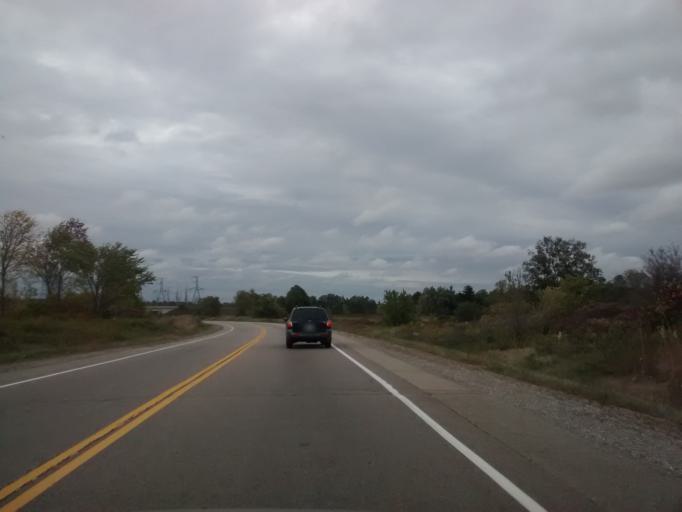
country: CA
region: Ontario
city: Ancaster
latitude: 43.0632
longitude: -79.9805
